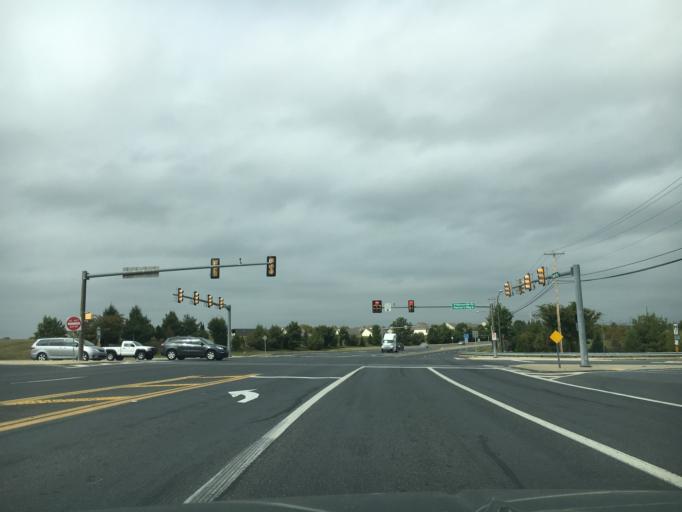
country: US
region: Pennsylvania
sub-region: Northampton County
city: Bath
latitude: 40.6819
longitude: -75.3893
